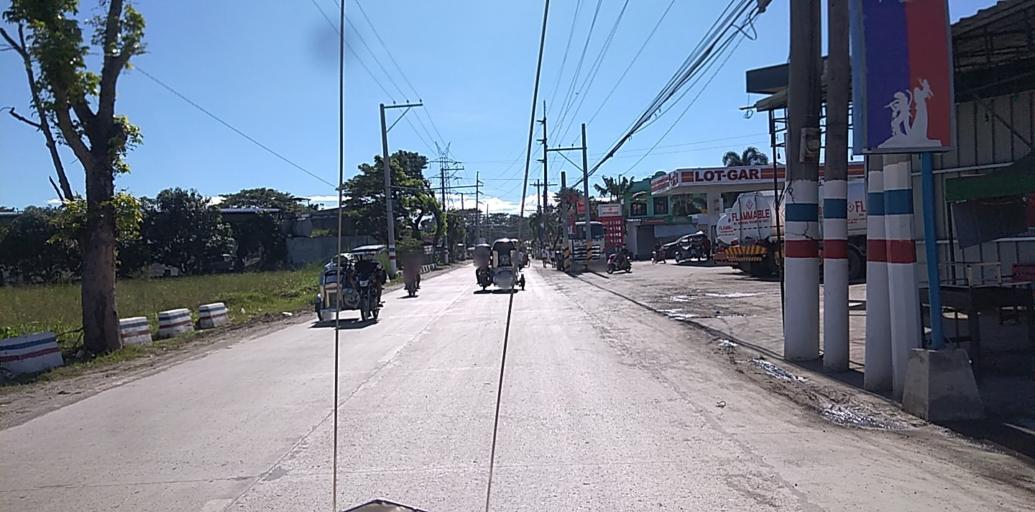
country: PH
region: Central Luzon
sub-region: Province of Pampanga
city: San Luis
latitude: 15.0441
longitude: 120.7886
